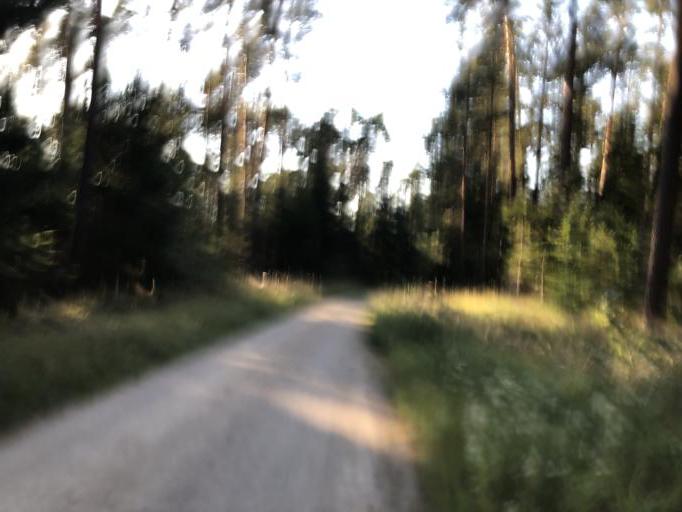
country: DE
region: Bavaria
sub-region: Regierungsbezirk Mittelfranken
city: Uttenreuth
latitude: 49.5611
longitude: 11.0877
